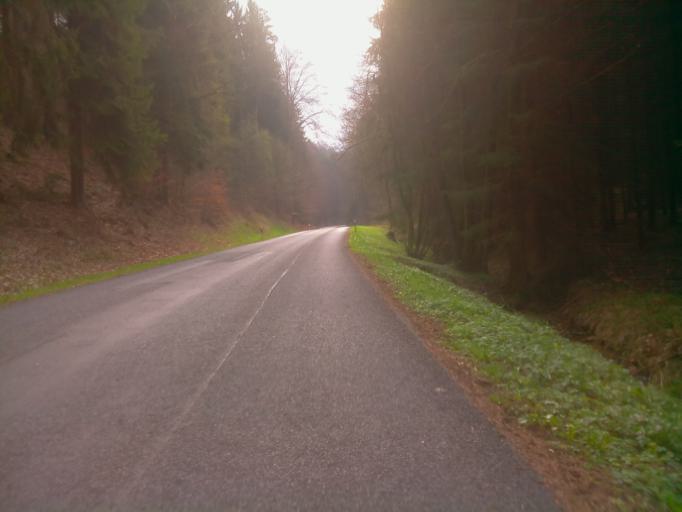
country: DE
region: Thuringia
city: Grosseutersdorf
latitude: 50.7688
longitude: 11.5688
